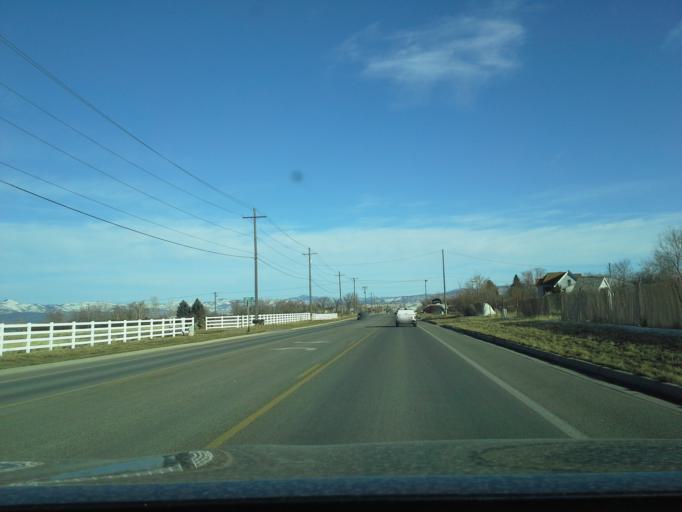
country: US
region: Montana
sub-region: Lewis and Clark County
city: Helena Valley Southeast
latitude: 46.6168
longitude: -111.9322
